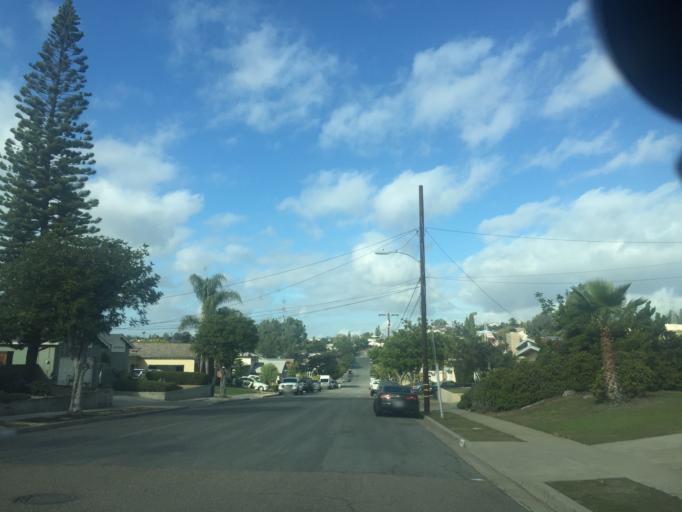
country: US
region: California
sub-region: San Diego County
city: San Diego
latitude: 32.7801
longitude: -117.1506
